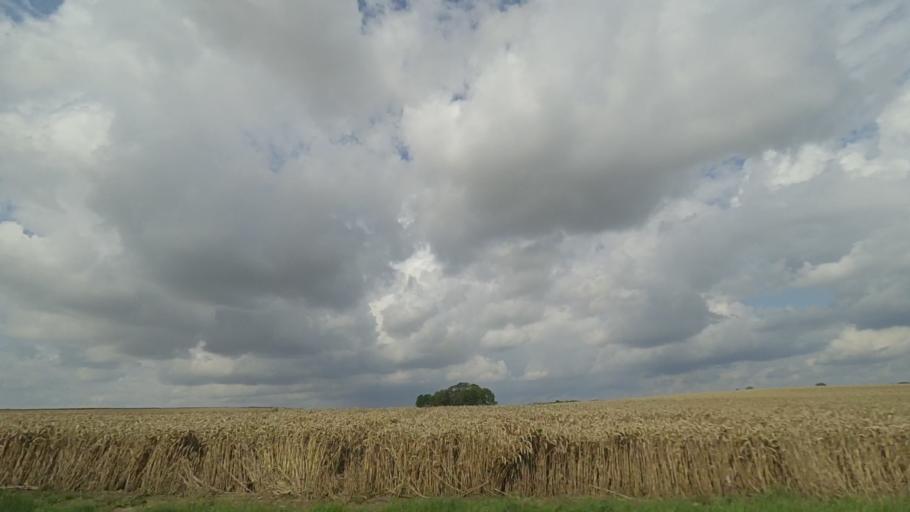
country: DK
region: Central Jutland
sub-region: Norddjurs Kommune
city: Allingabro
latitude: 56.5344
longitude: 10.3611
